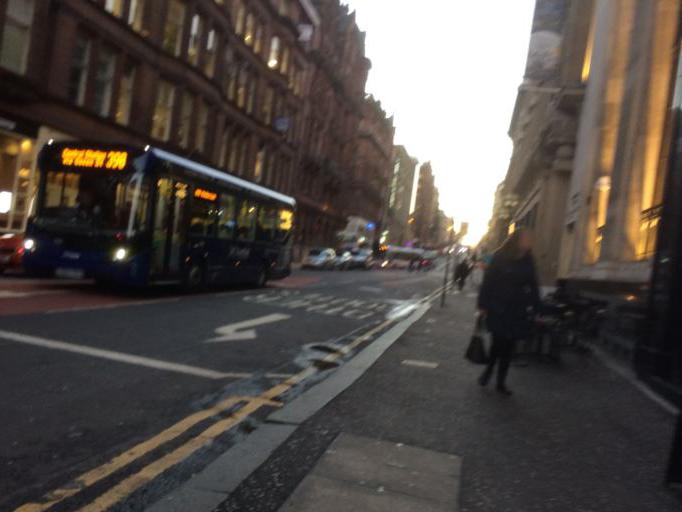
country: GB
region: Scotland
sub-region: Glasgow City
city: Glasgow
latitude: 55.8623
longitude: -4.2550
